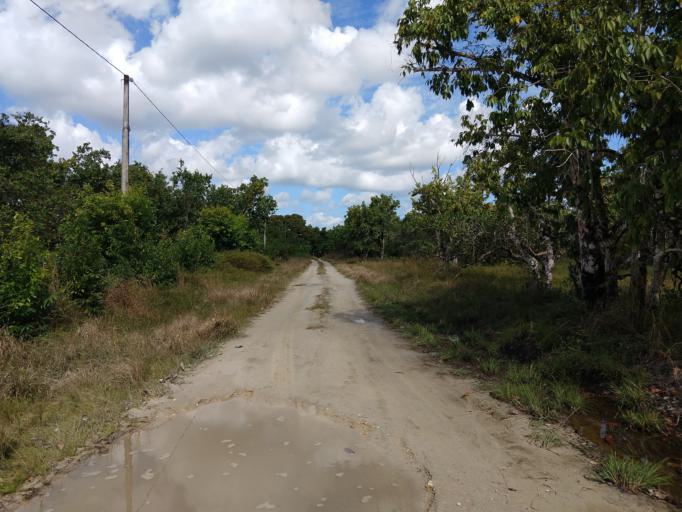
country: BZ
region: Belize
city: Belize City
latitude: 17.5712
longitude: -88.4122
